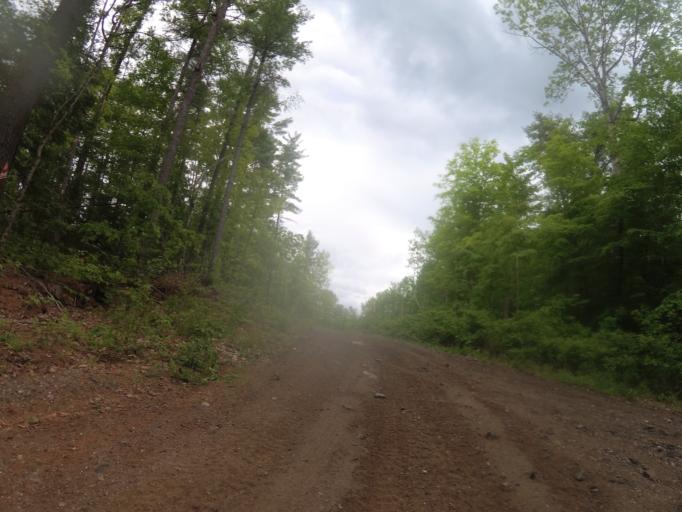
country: CA
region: Ontario
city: Renfrew
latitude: 45.1174
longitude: -76.8224
